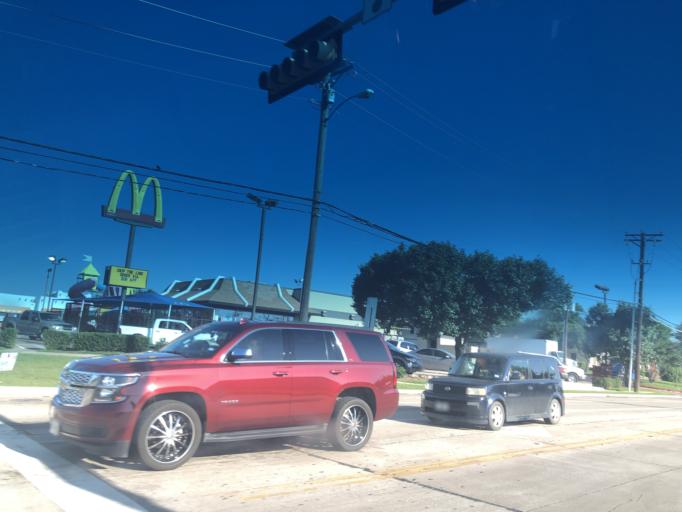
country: US
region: Texas
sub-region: Dallas County
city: Grand Prairie
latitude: 32.7096
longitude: -97.0024
